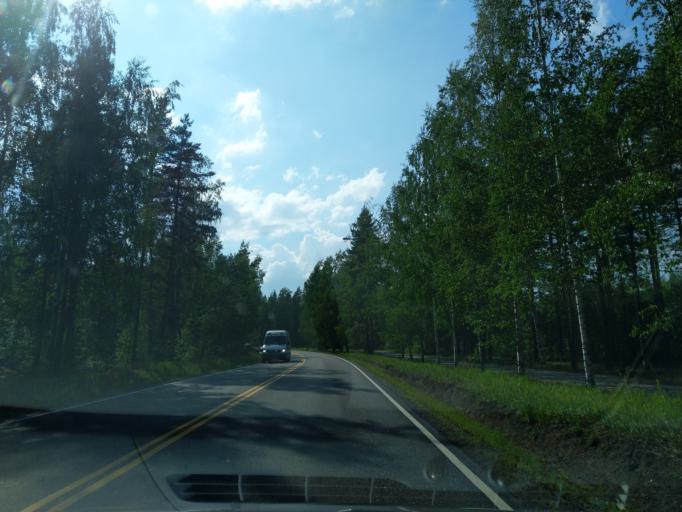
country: FI
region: Kymenlaakso
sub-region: Kouvola
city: Kouvola
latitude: 60.8849
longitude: 26.7868
